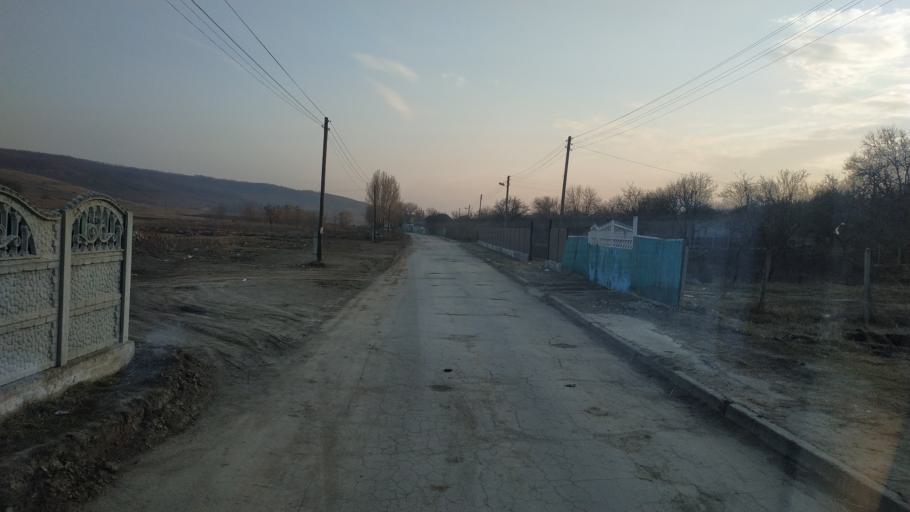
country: MD
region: Hincesti
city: Dancu
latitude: 46.7098
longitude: 28.3454
